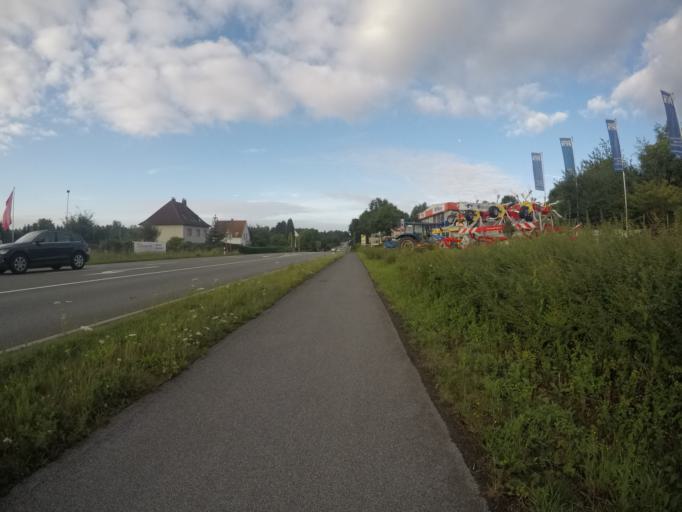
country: DE
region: North Rhine-Westphalia
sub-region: Regierungsbezirk Detmold
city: Herford
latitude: 52.0713
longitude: 8.6143
